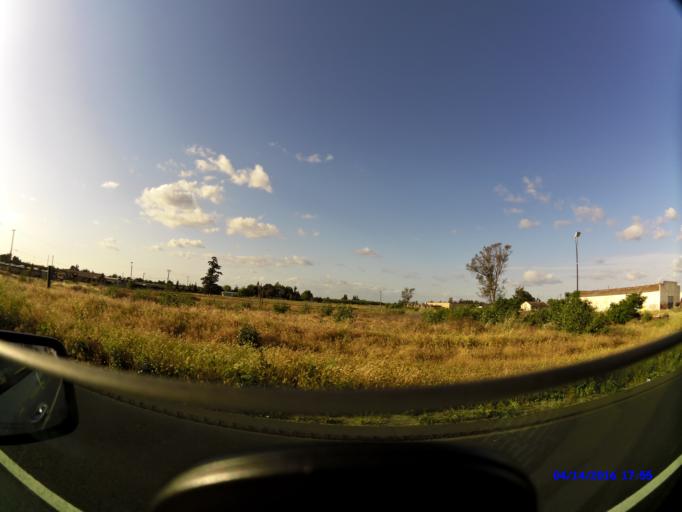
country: US
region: California
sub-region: Stanislaus County
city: Del Rio
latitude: 37.7114
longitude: -121.0052
